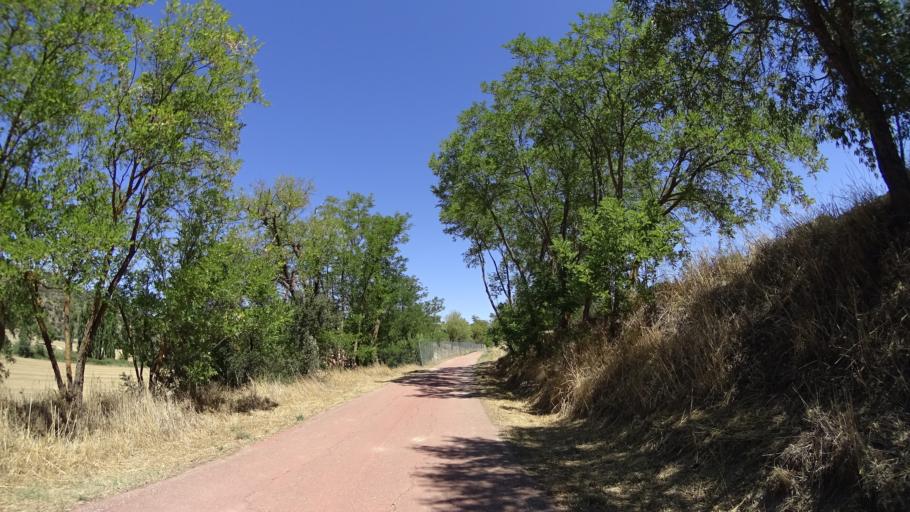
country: ES
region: Madrid
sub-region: Provincia de Madrid
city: Ambite
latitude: 40.3077
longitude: -3.1919
